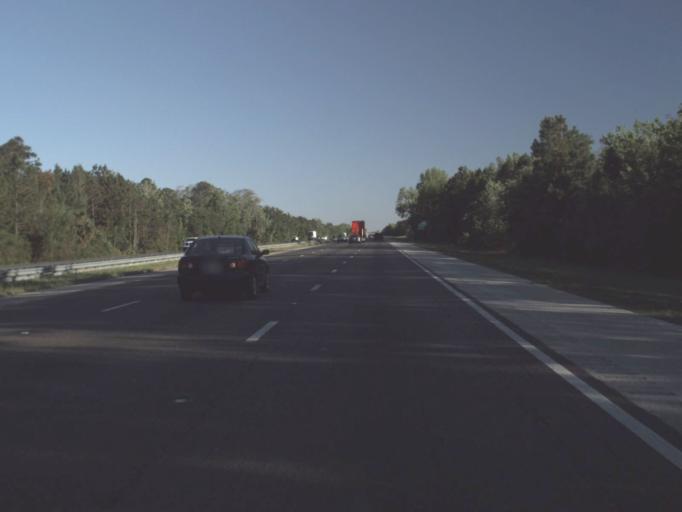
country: US
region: Florida
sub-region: Flagler County
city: Palm Coast
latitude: 29.6281
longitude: -81.2637
